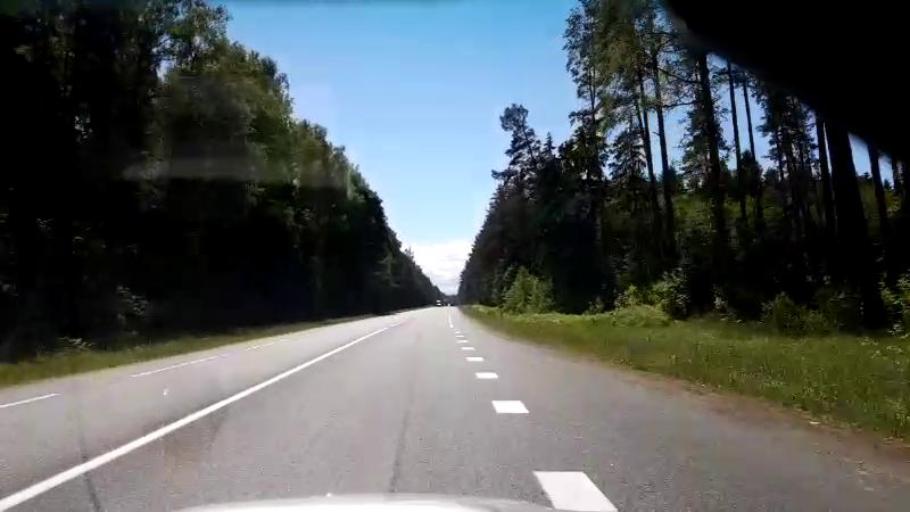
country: LV
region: Saulkrastu
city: Saulkrasti
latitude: 57.3644
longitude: 24.4371
